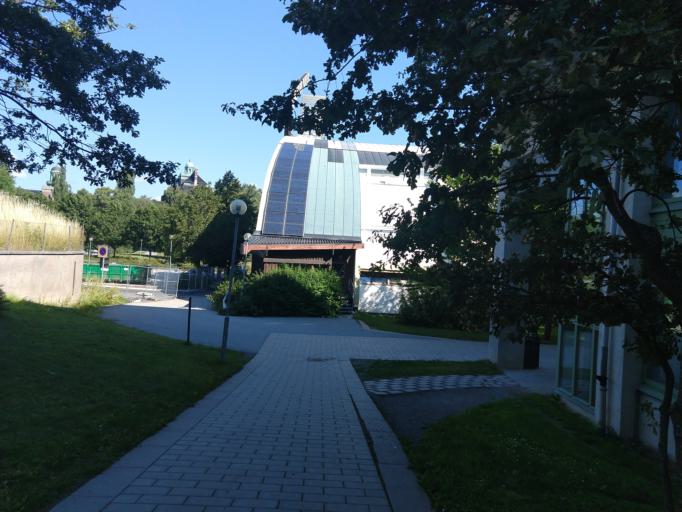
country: SE
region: Stockholm
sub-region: Norrtalje Kommun
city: Bergshamra
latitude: 59.3661
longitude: 18.0571
